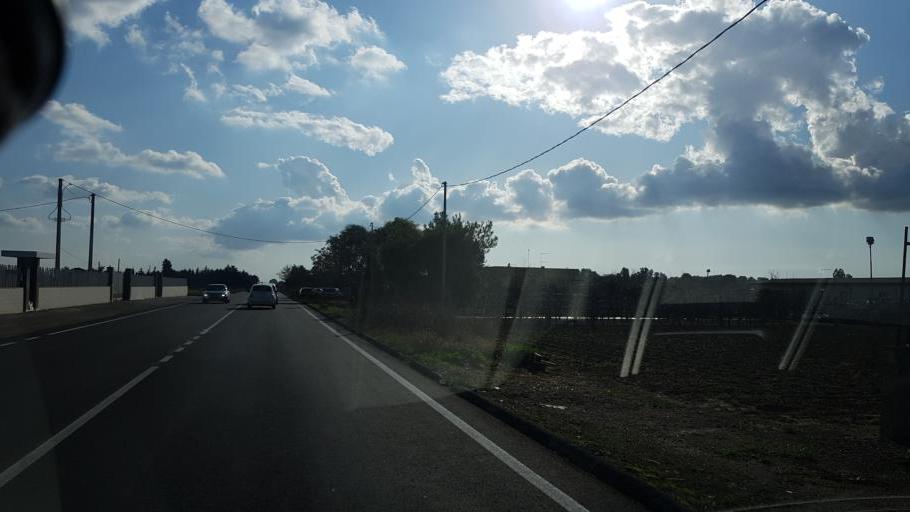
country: IT
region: Apulia
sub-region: Provincia di Lecce
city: Salice Salentino
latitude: 40.3717
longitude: 17.9668
